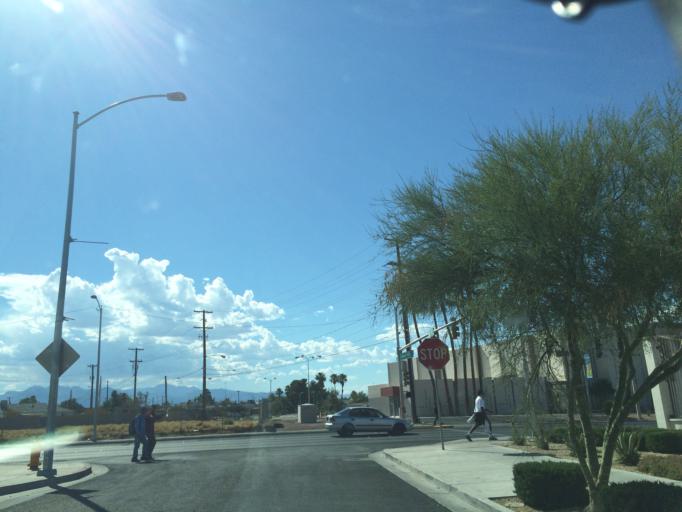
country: US
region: Nevada
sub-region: Clark County
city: Las Vegas
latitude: 36.1772
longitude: -115.1352
